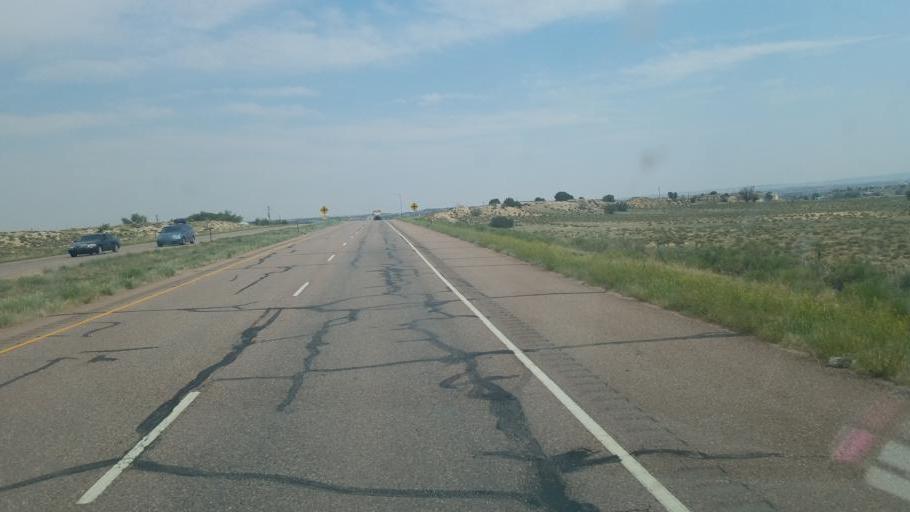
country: US
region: Colorado
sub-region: Fremont County
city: Penrose
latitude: 38.3938
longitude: -104.9715
